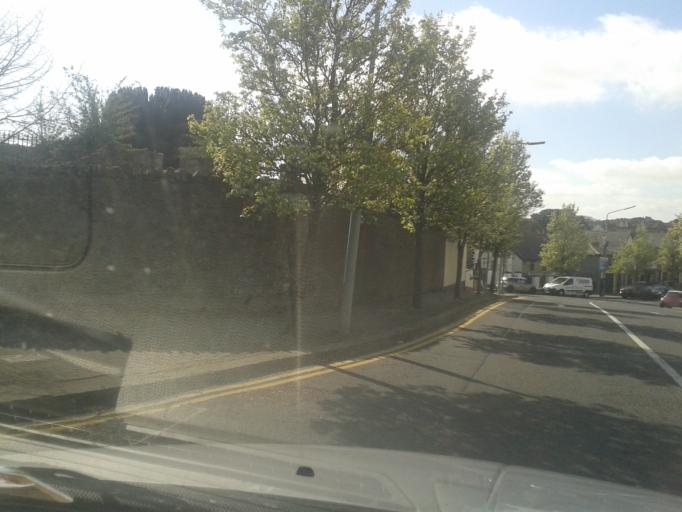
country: IE
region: Leinster
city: Raheny
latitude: 53.3803
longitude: -6.1750
